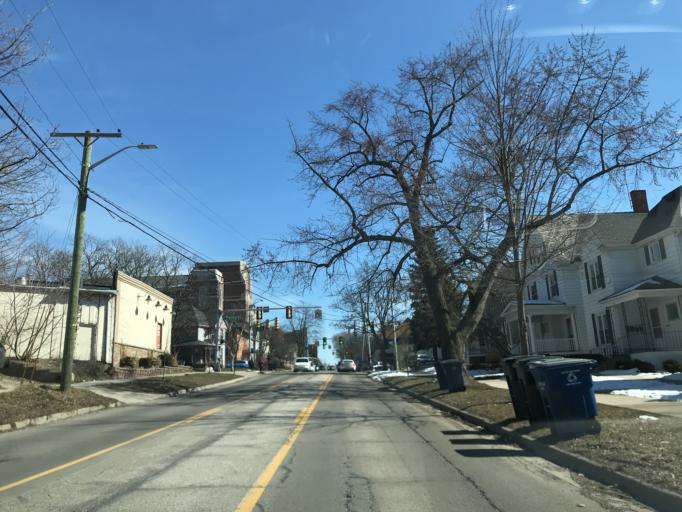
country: US
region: Michigan
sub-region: Washtenaw County
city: Ann Arbor
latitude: 42.2718
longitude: -83.7428
